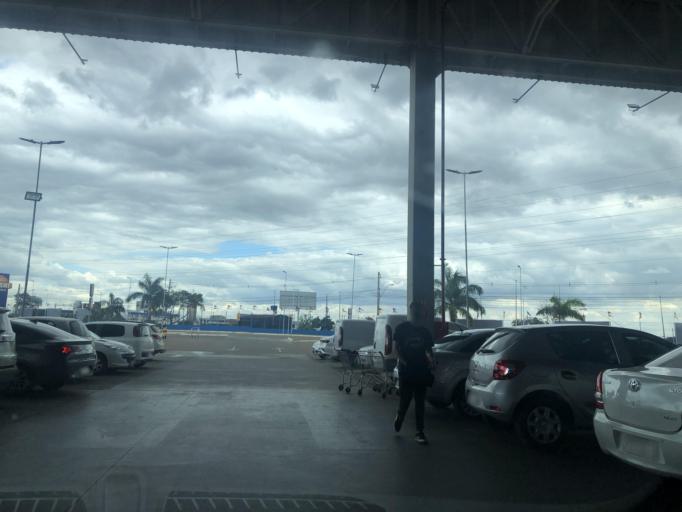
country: BR
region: Federal District
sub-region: Brasilia
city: Brasilia
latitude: -15.8751
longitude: -48.0253
